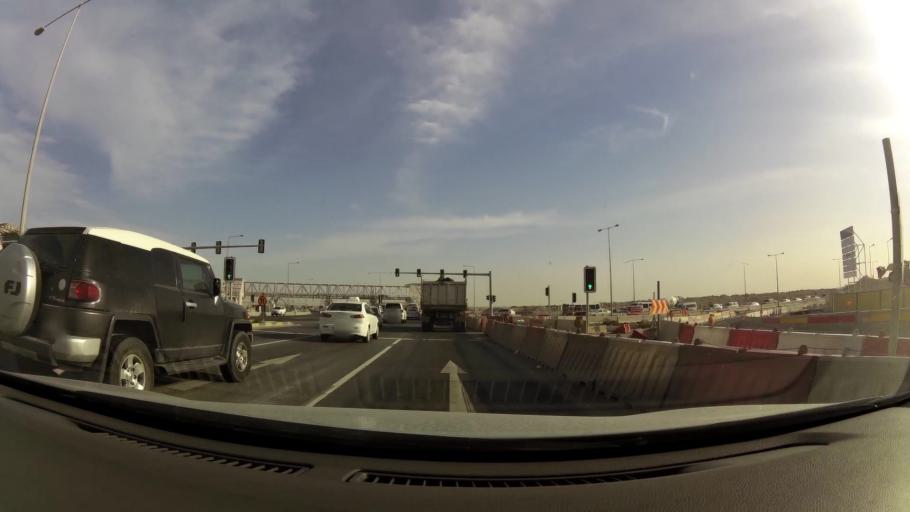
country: QA
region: Al Wakrah
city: Al Wakrah
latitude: 25.2130
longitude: 51.5844
